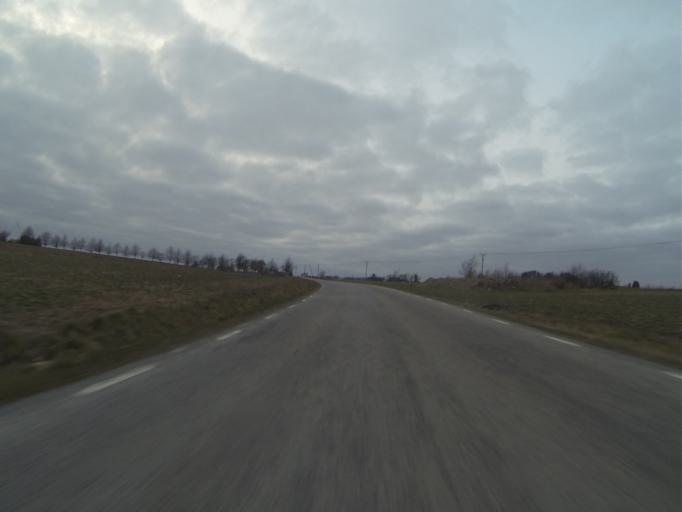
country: SE
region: Skane
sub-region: Lunds Kommun
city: Genarp
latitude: 55.6385
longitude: 13.3648
